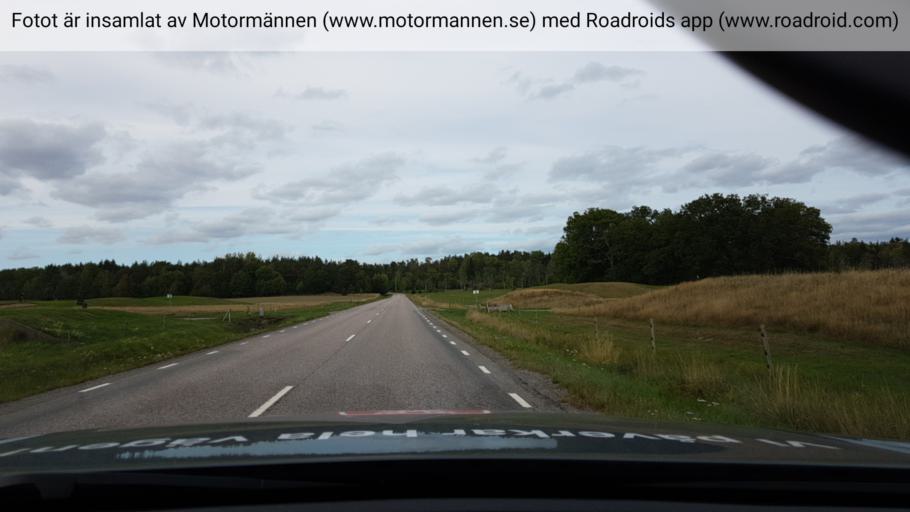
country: SE
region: Stockholm
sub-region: Haninge Kommun
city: Haninge
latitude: 59.1106
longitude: 18.1888
